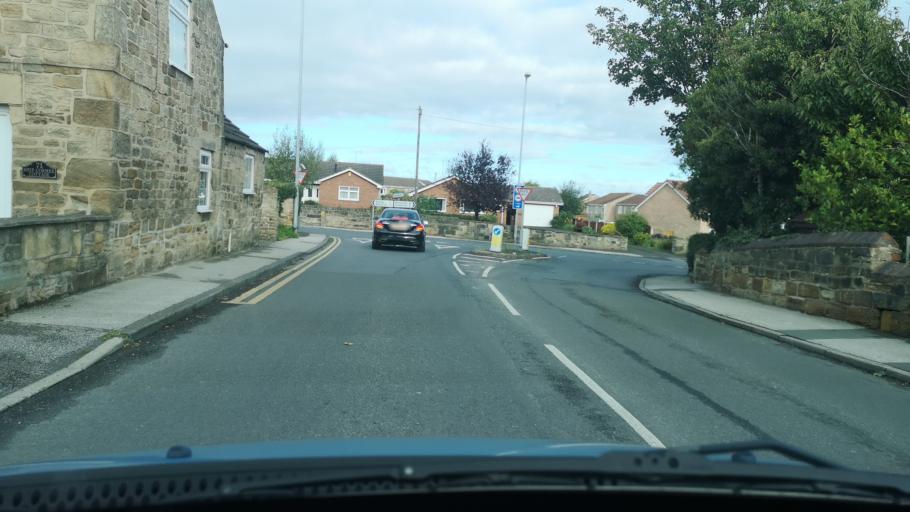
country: GB
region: England
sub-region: City and Borough of Wakefield
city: Normanton
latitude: 53.7069
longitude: -1.4376
